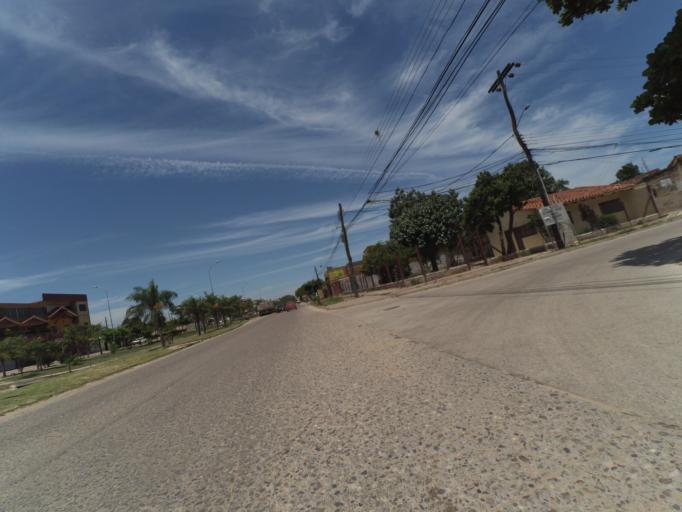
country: BO
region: Santa Cruz
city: Santa Cruz de la Sierra
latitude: -17.8089
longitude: -63.2160
